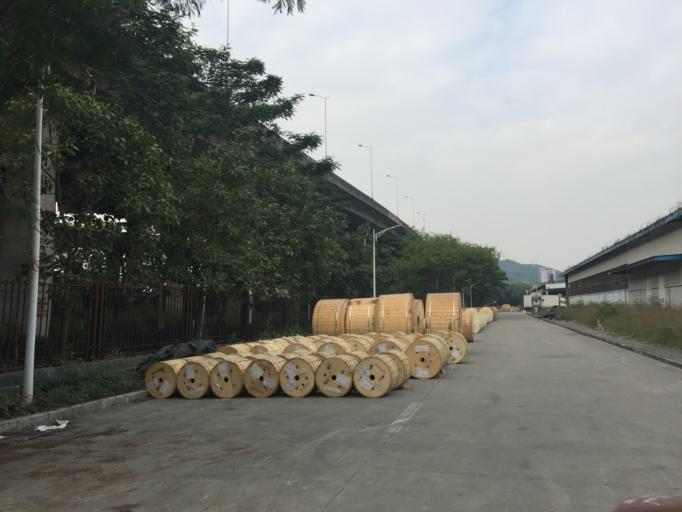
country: CN
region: Guangdong
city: Xin'an
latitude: 22.5799
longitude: 113.9256
